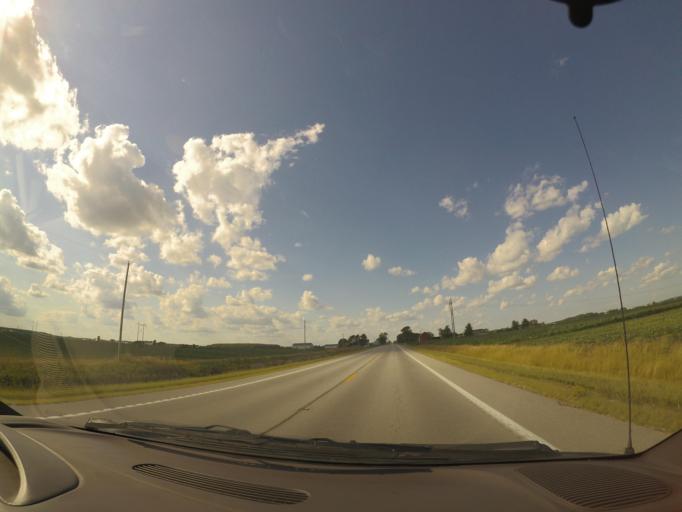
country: US
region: Ohio
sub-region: Wood County
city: Pemberville
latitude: 41.3608
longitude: -83.4169
